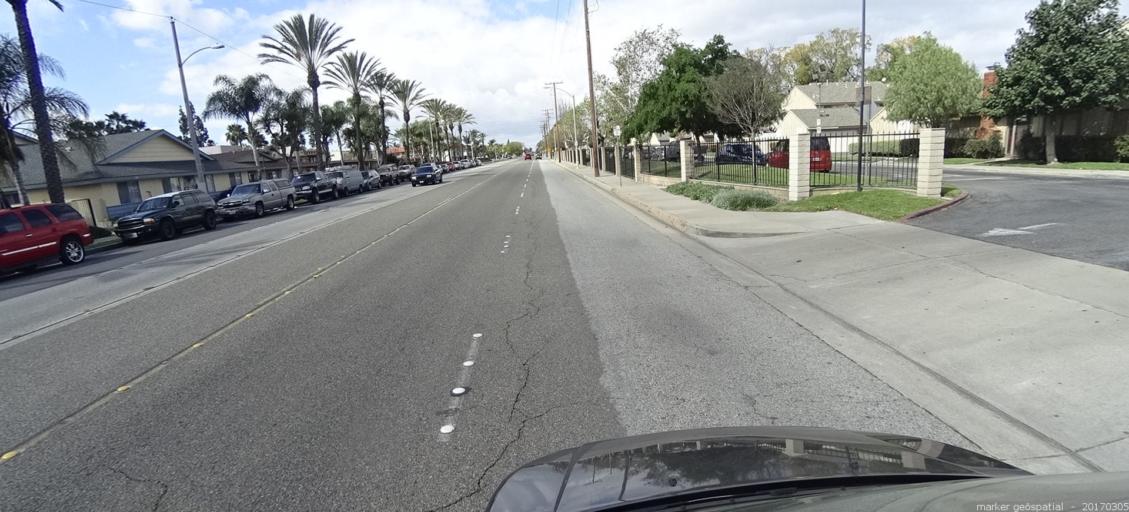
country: US
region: California
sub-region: Orange County
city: Anaheim
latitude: 33.8106
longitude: -117.9296
